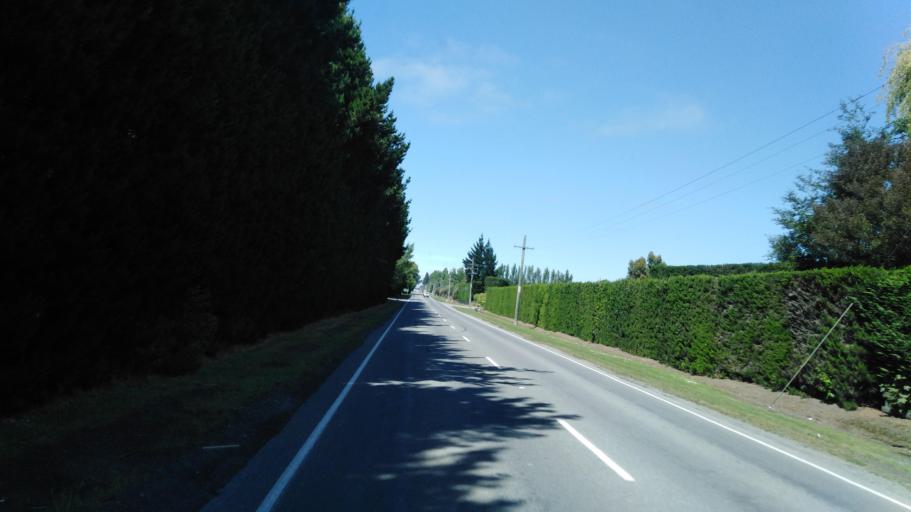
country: NZ
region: Canterbury
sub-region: Selwyn District
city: Prebbleton
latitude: -43.5157
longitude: 172.5071
